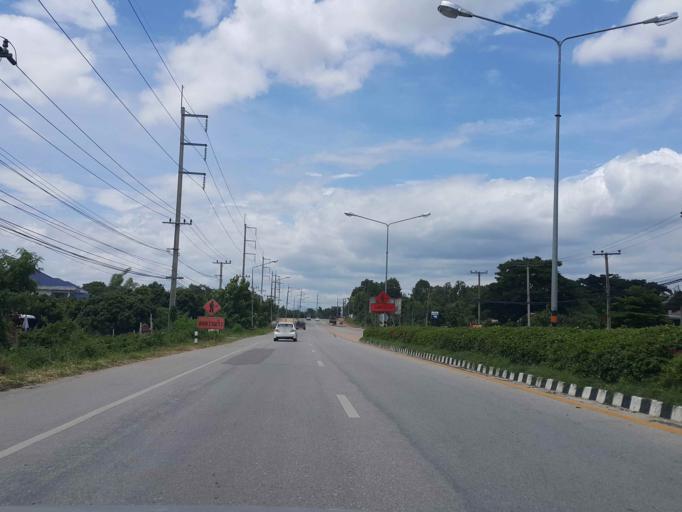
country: TH
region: Lamphun
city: Ban Hong
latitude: 18.3182
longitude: 98.8200
